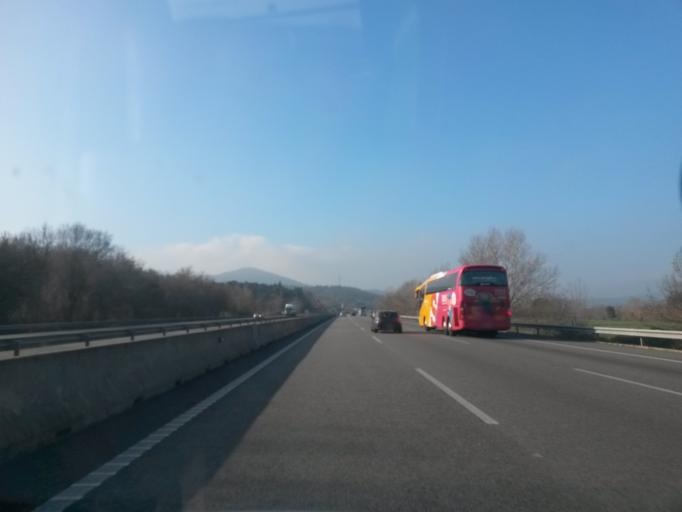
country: ES
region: Catalonia
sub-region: Provincia de Girona
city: Breda
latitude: 41.7194
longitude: 2.5688
